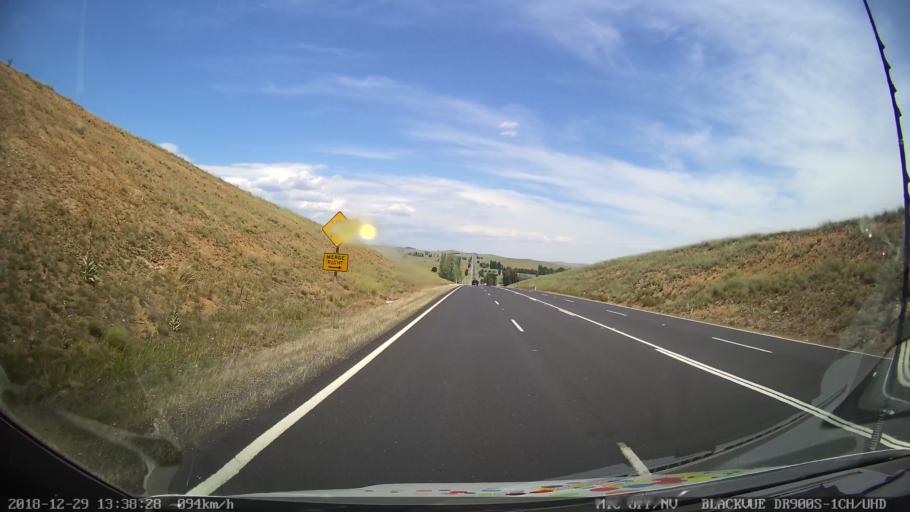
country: AU
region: New South Wales
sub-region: Cooma-Monaro
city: Cooma
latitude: -35.9988
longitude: 149.1417
